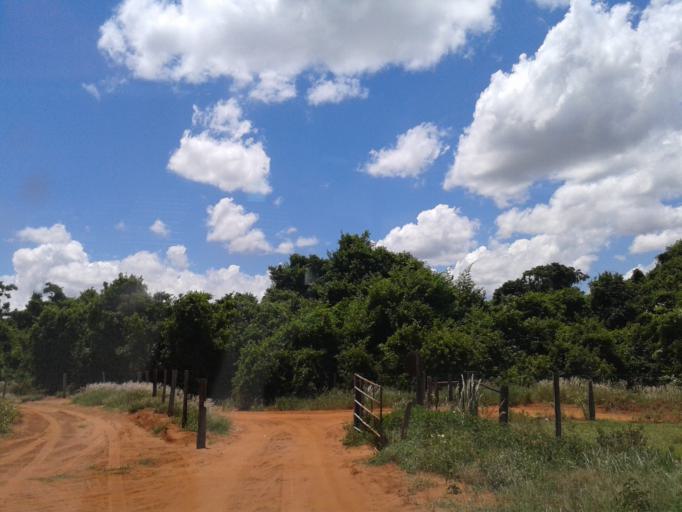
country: BR
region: Minas Gerais
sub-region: Centralina
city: Centralina
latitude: -18.6977
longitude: -49.1577
